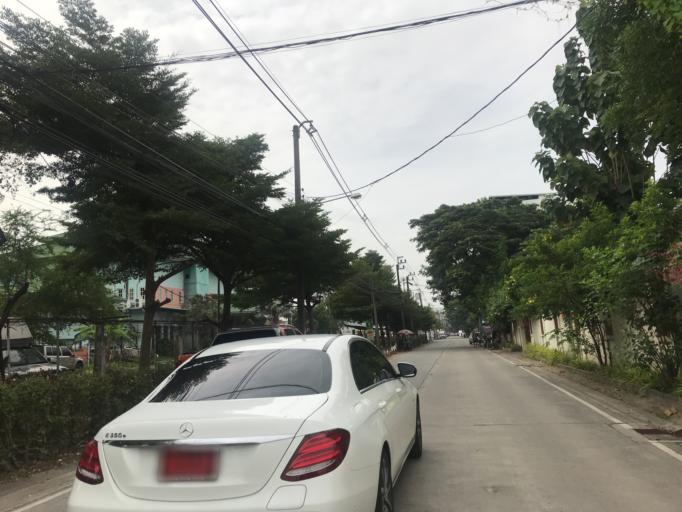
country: TH
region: Bangkok
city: Bang Kapi
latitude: 13.7472
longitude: 100.6352
